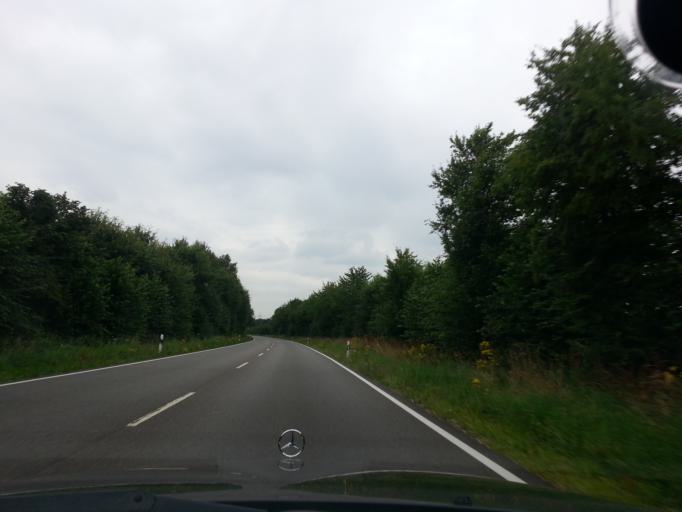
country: DE
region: North Rhine-Westphalia
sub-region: Regierungsbezirk Munster
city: Raesfeld
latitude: 51.7758
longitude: 6.8493
